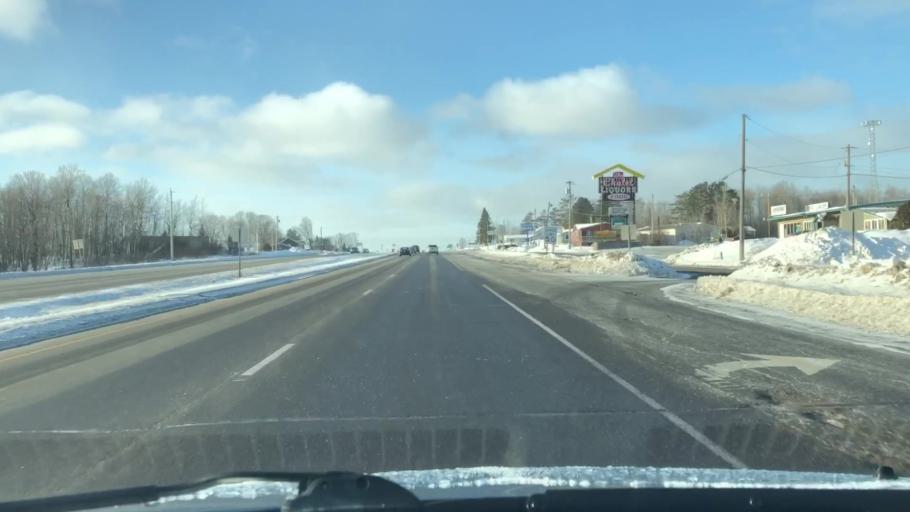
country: US
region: Minnesota
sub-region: Saint Louis County
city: Hermantown
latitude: 46.8232
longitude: -92.1884
